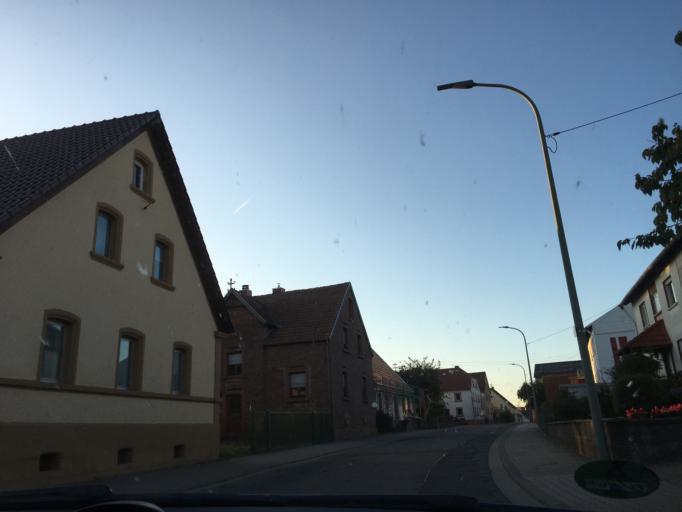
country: DE
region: Rheinland-Pfalz
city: Hermersberg
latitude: 49.3189
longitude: 7.6340
